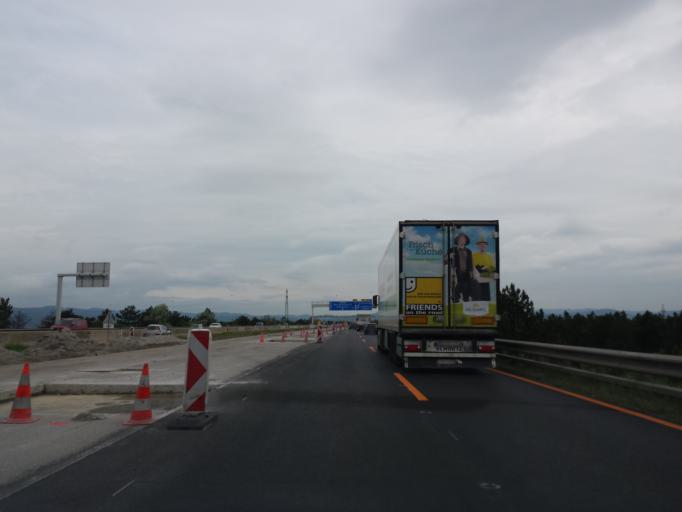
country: AT
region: Lower Austria
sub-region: Wiener Neustadt Stadt
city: Wiener Neustadt
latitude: 47.8002
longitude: 16.2014
